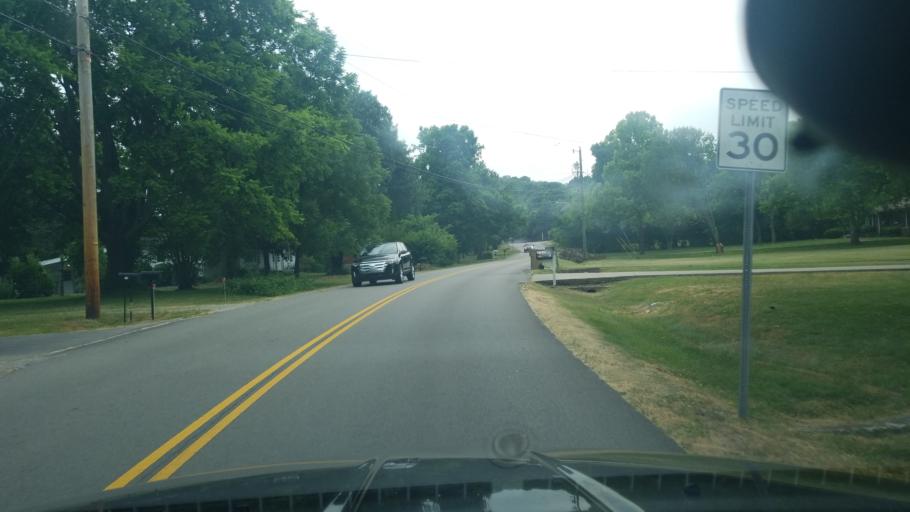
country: US
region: Tennessee
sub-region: Davidson County
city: Goodlettsville
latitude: 36.2644
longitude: -86.7424
